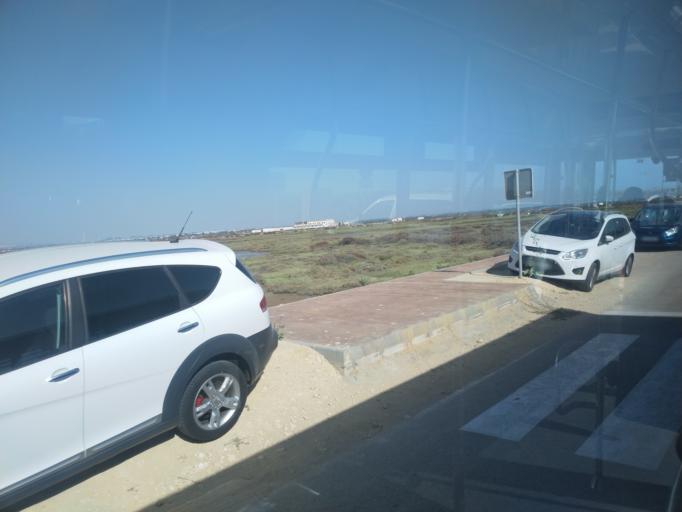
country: ES
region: Andalusia
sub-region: Provincia de Cadiz
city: San Fernando
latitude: 36.4235
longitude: -6.2264
